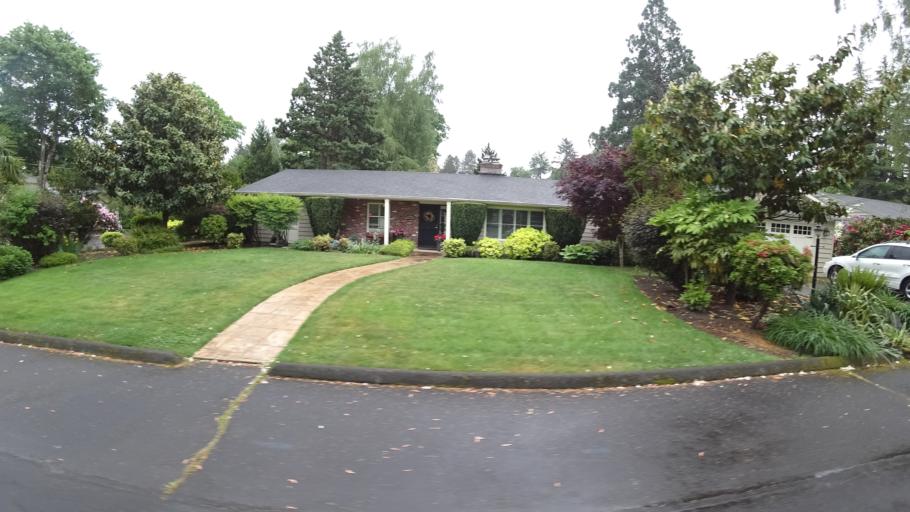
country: US
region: Oregon
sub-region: Washington County
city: Raleigh Hills
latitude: 45.4789
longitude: -122.7678
